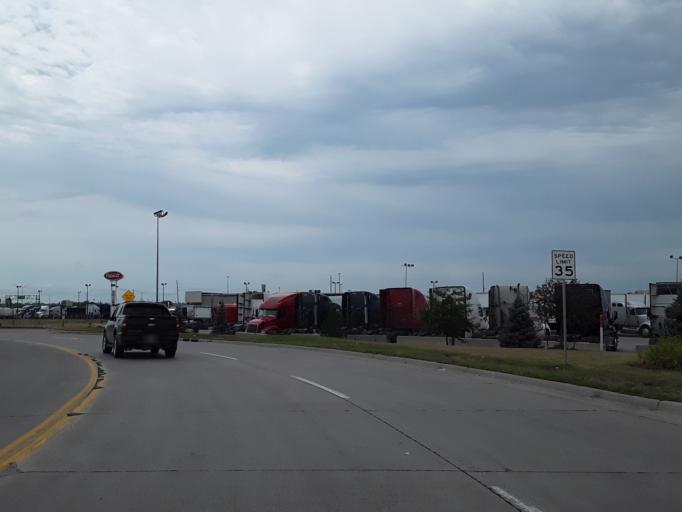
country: US
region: Iowa
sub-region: Pottawattamie County
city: Council Bluffs
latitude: 41.2352
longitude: -95.8802
